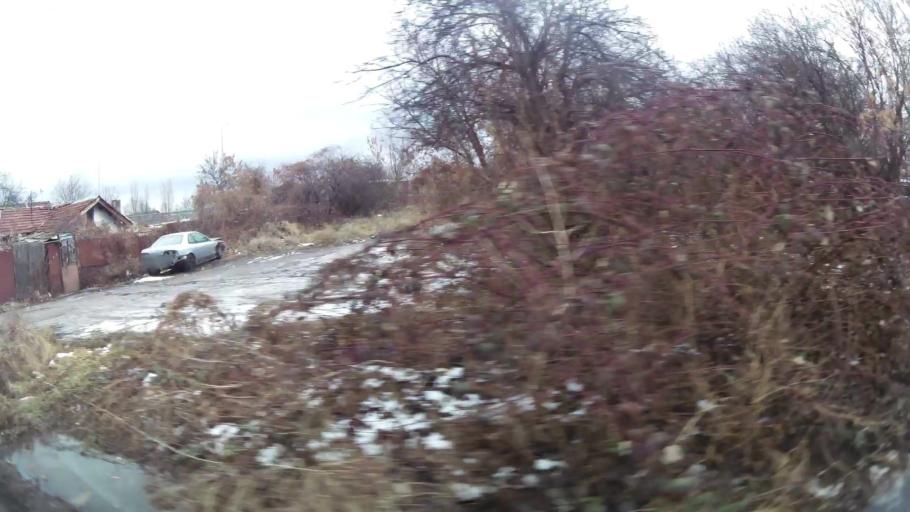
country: BG
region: Sofia-Capital
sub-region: Stolichna Obshtina
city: Sofia
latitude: 42.7260
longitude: 23.2810
